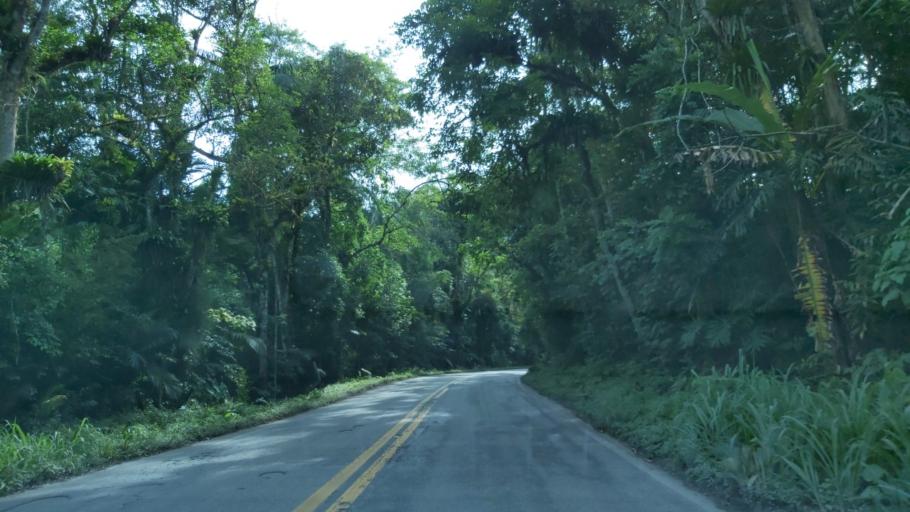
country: BR
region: Sao Paulo
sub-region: Miracatu
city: Miracatu
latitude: -24.0587
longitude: -47.5764
